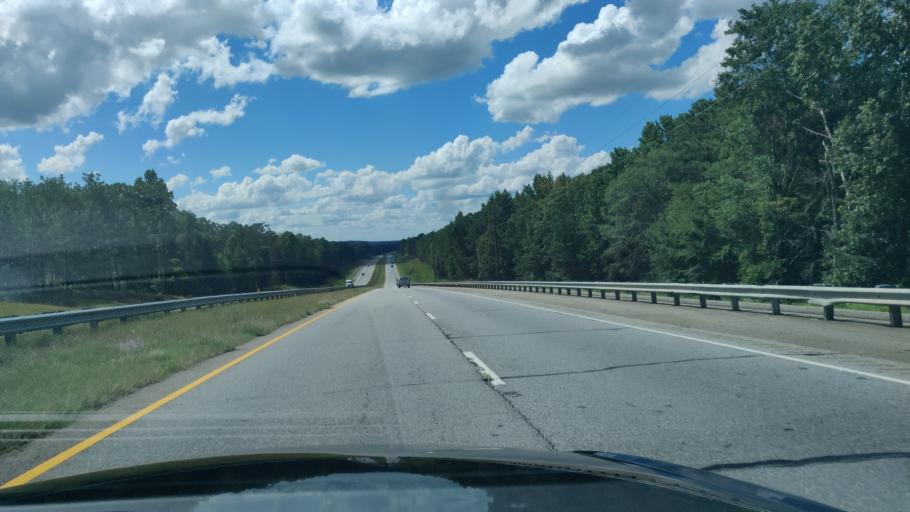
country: US
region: Georgia
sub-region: Chattahoochee County
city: Cusseta
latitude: 32.3830
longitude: -84.8702
